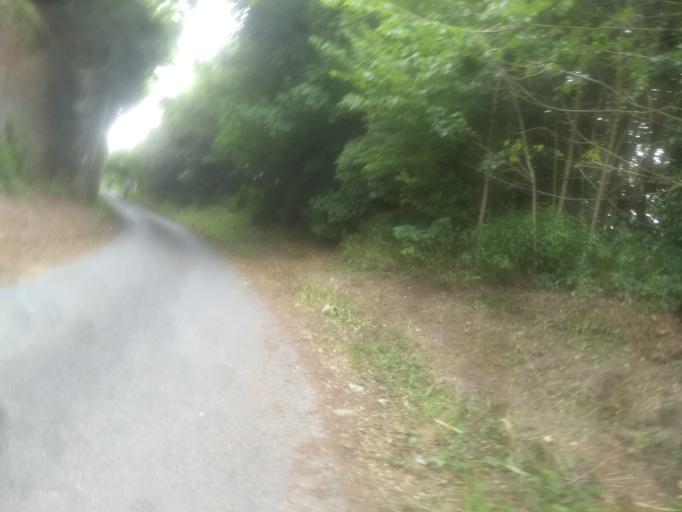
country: FR
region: Nord-Pas-de-Calais
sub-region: Departement du Pas-de-Calais
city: Mont-Saint-Eloi
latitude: 50.3466
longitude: 2.6898
